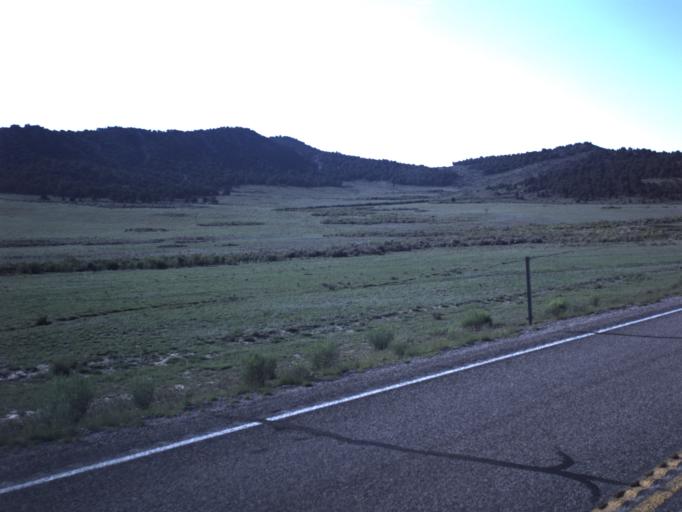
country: US
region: Utah
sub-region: Wayne County
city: Loa
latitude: 38.6852
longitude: -111.3977
